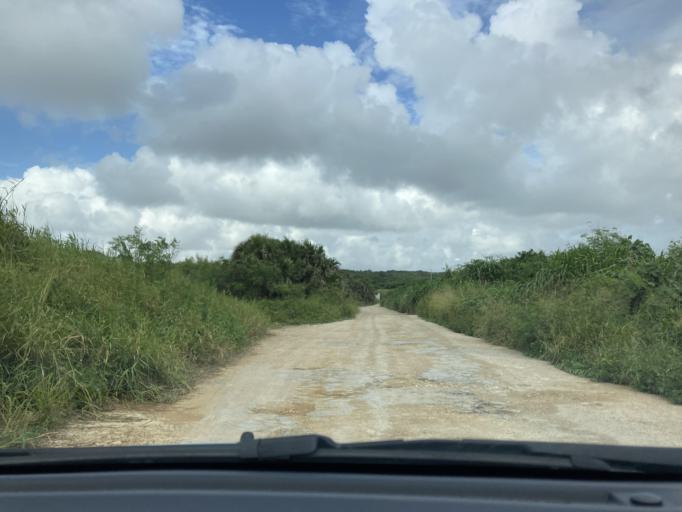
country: JP
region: Okinawa
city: Itoman
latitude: 26.0801
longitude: 127.6834
